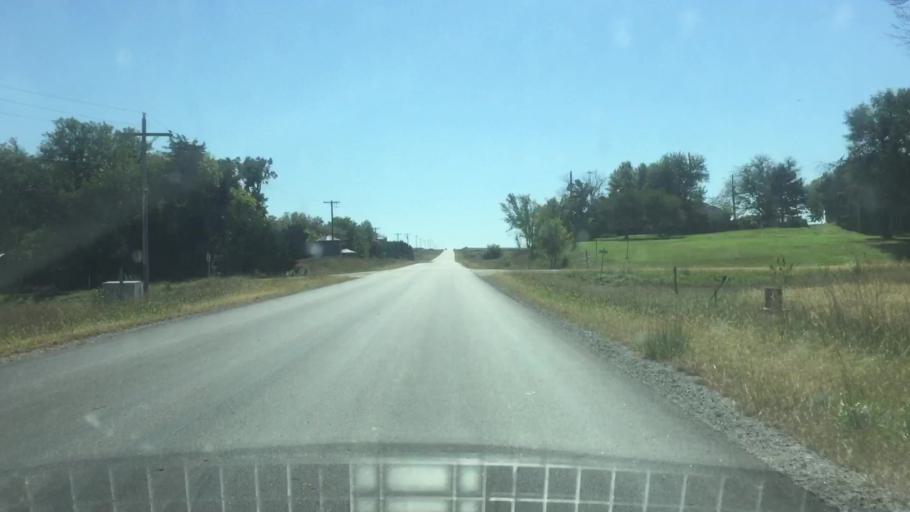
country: US
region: Kansas
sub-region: Marshall County
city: Marysville
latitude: 39.9294
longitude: -96.6009
